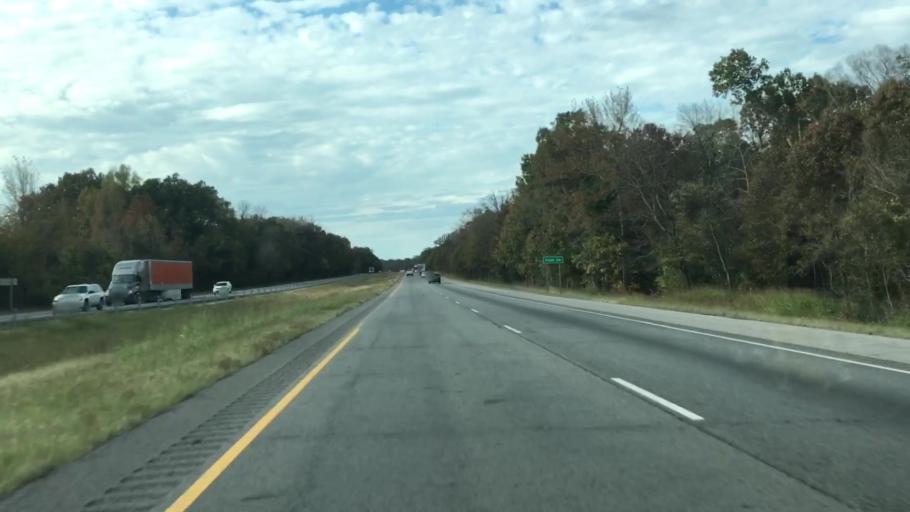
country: US
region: Arkansas
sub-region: Pope County
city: Atkins
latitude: 35.2372
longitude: -92.8538
